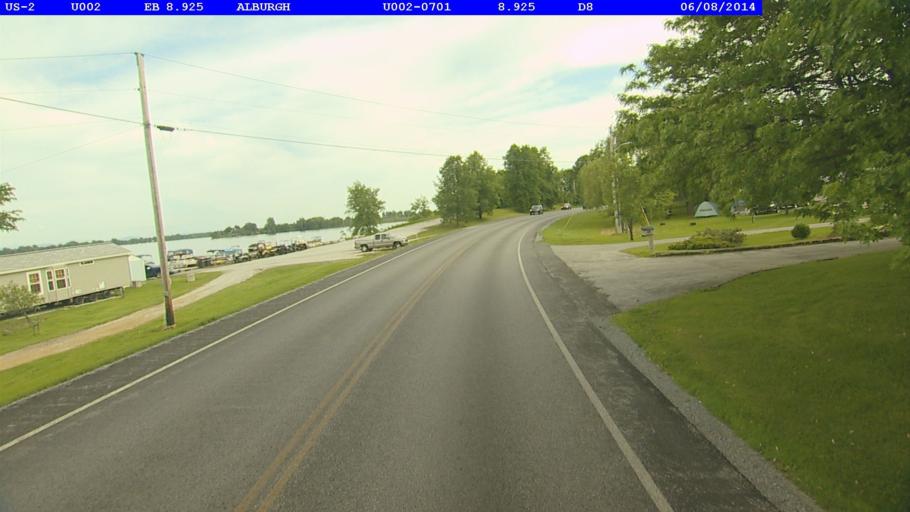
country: US
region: Vermont
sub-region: Grand Isle County
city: North Hero
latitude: 44.9219
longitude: -73.2738
